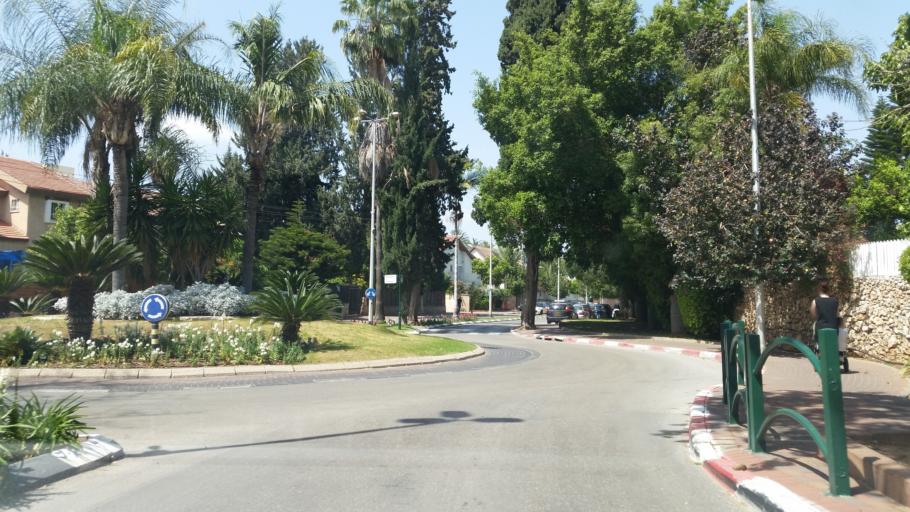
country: IL
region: Central District
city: Ra'anana
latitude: 32.1836
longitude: 34.8819
